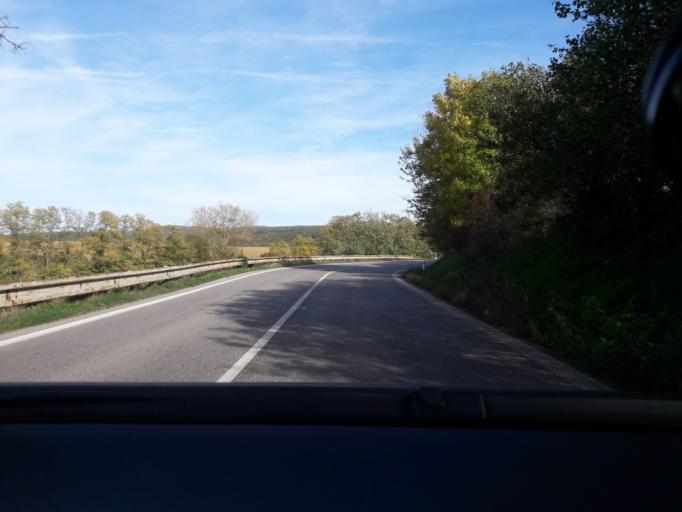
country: SK
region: Nitriansky
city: Levice
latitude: 48.2595
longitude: 18.7526
